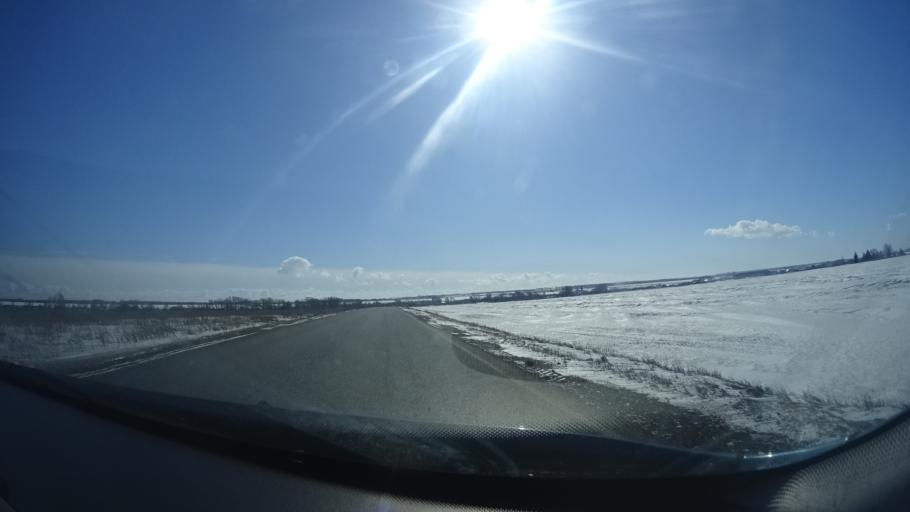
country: RU
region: Bashkortostan
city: Avdon
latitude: 54.5893
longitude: 55.8557
